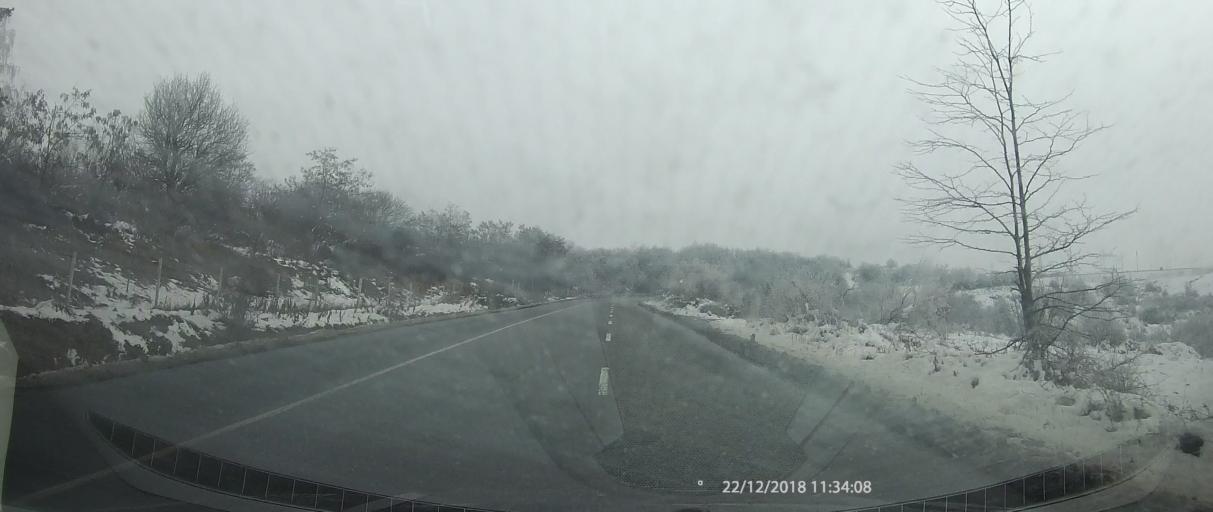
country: BG
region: Kyustendil
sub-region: Obshtina Dupnitsa
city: Dupnitsa
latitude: 42.2676
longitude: 23.0637
